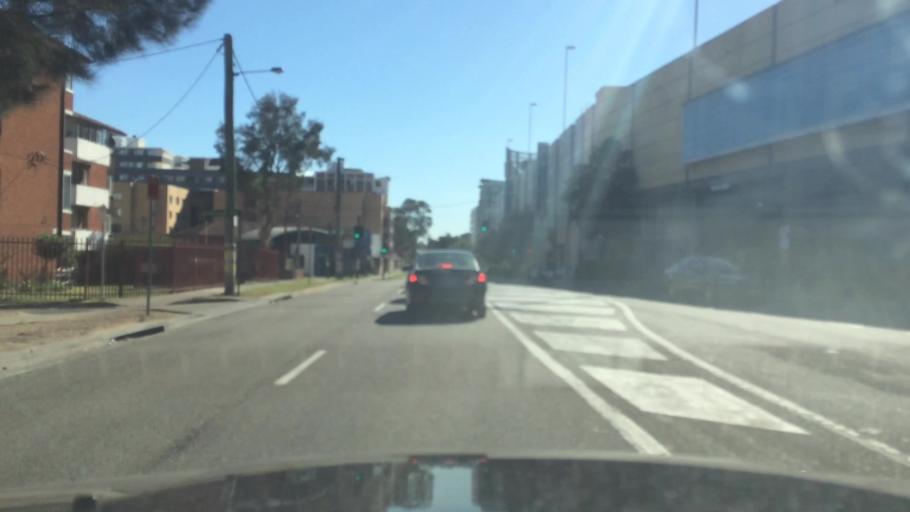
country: AU
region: New South Wales
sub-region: Fairfield
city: Liverpool
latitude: -33.9192
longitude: 150.9219
